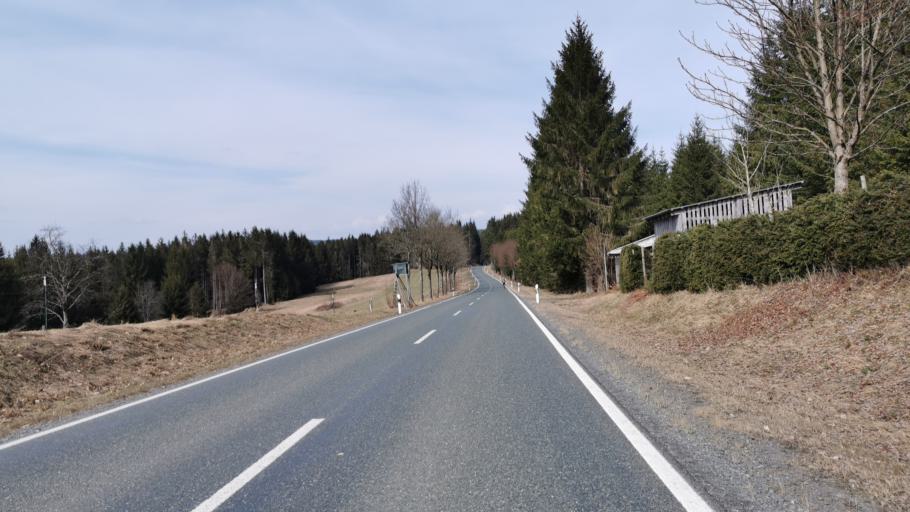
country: DE
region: Bavaria
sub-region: Upper Franconia
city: Tschirn
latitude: 50.4131
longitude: 11.4523
